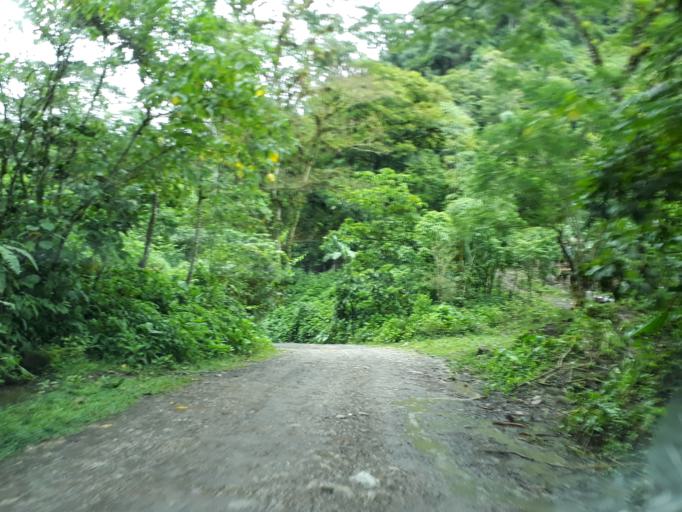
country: CO
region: Boyaca
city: Santa Maria
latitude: 4.7570
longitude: -73.3143
